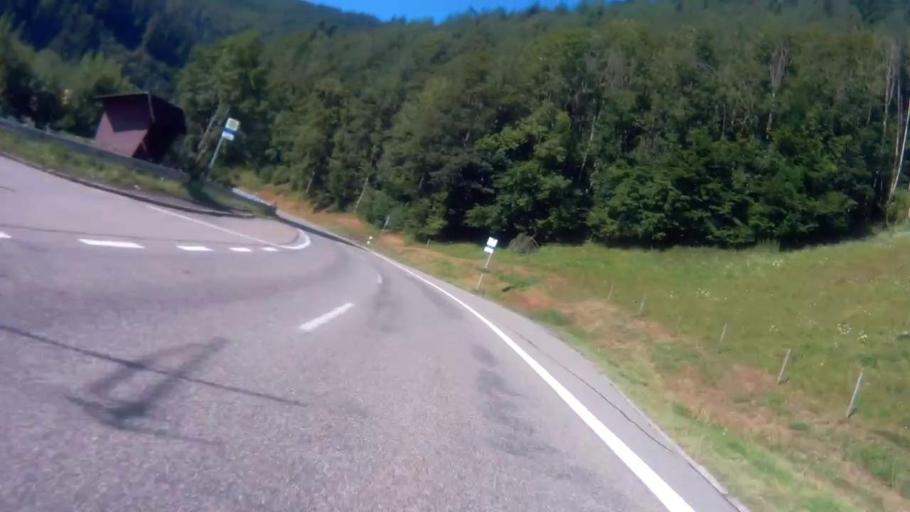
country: DE
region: Baden-Wuerttemberg
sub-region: Freiburg Region
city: Wembach
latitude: 47.7276
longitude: 7.8972
